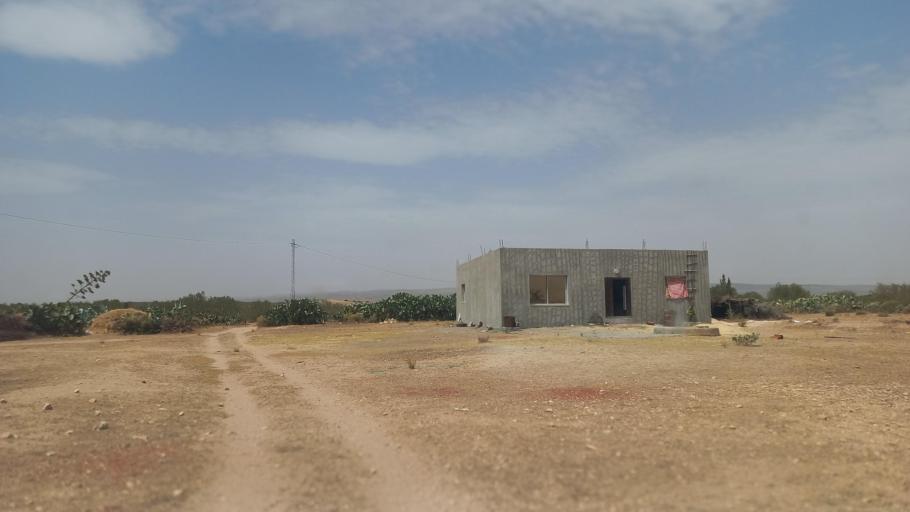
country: TN
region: Al Qasrayn
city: Kasserine
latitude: 35.2640
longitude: 8.9866
